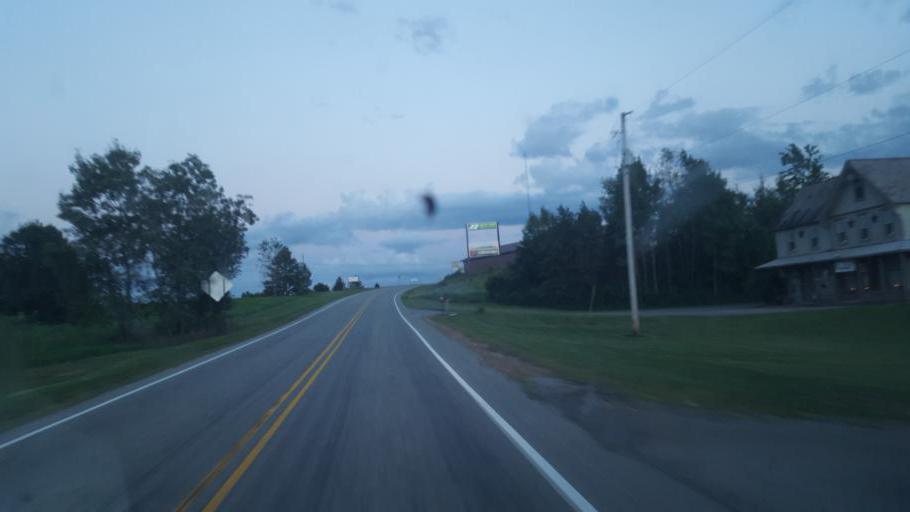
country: US
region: Pennsylvania
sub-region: Clarion County
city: Knox
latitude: 41.1908
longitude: -79.5464
